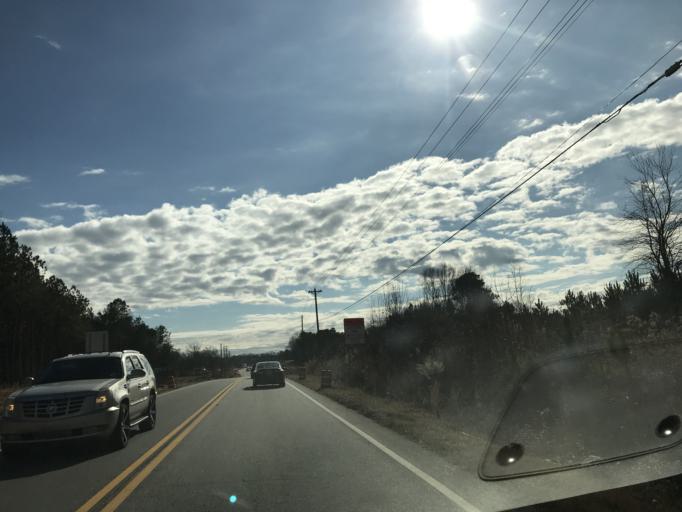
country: US
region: Georgia
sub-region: Paulding County
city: Hiram
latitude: 33.8605
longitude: -84.7605
